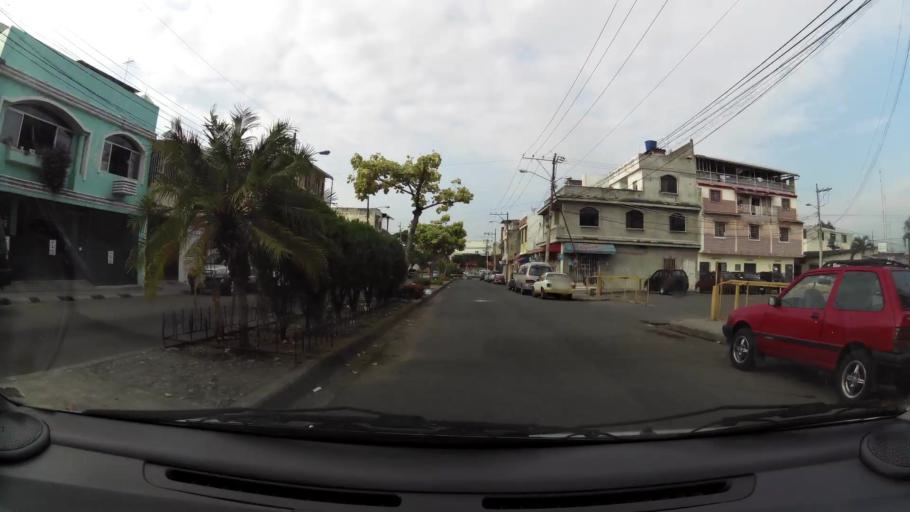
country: EC
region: Guayas
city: Eloy Alfaro
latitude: -2.1311
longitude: -79.8914
